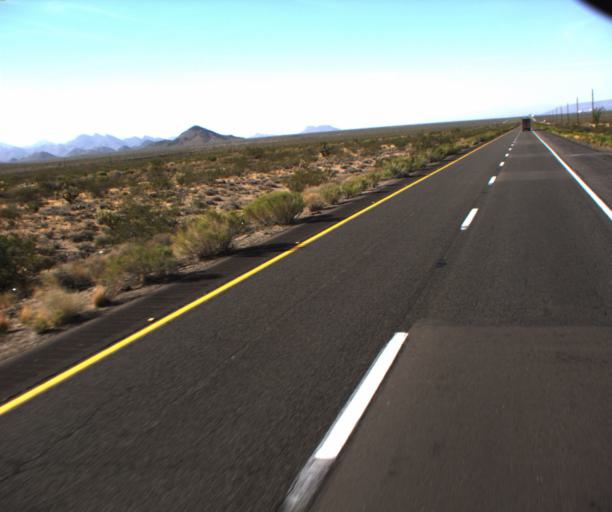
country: US
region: Arizona
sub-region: Mohave County
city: Kingman
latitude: 35.1024
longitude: -114.1179
